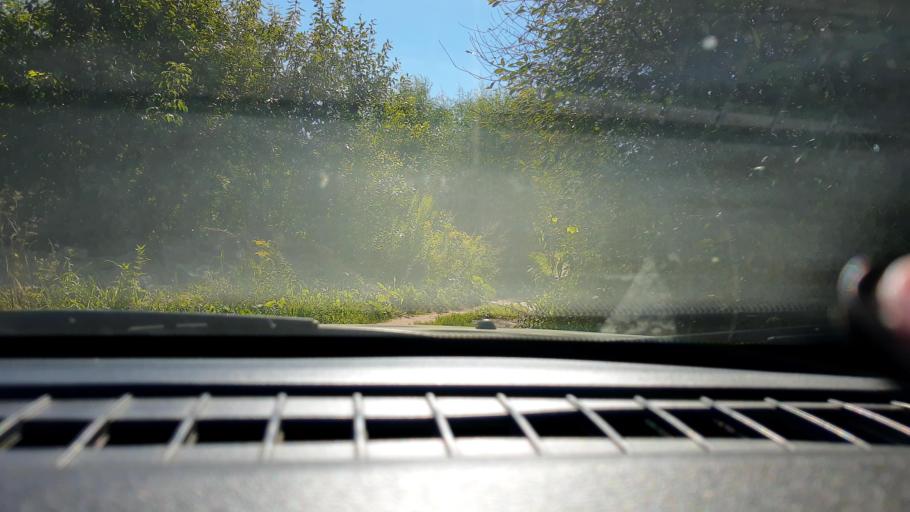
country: RU
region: Nizjnij Novgorod
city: Afonino
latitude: 56.2285
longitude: 44.0457
